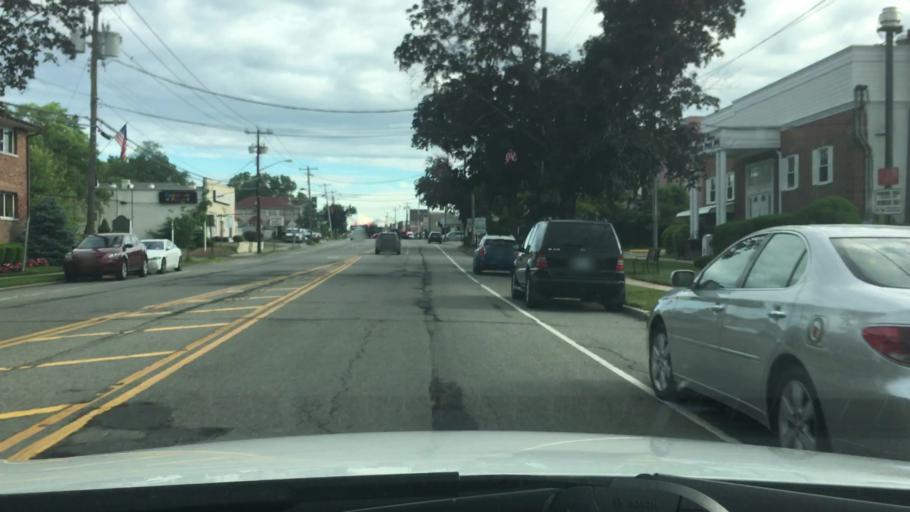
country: US
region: New York
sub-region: Nassau County
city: Williston Park
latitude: 40.7648
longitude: -73.6470
